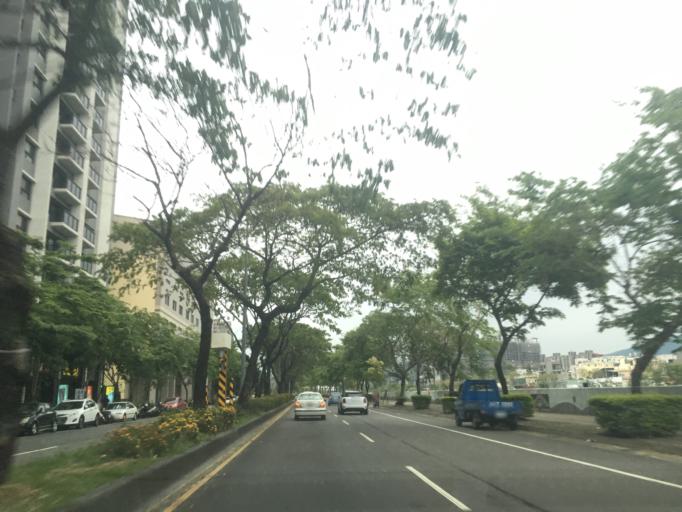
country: TW
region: Taiwan
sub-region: Taichung City
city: Taichung
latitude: 24.1527
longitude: 120.7246
